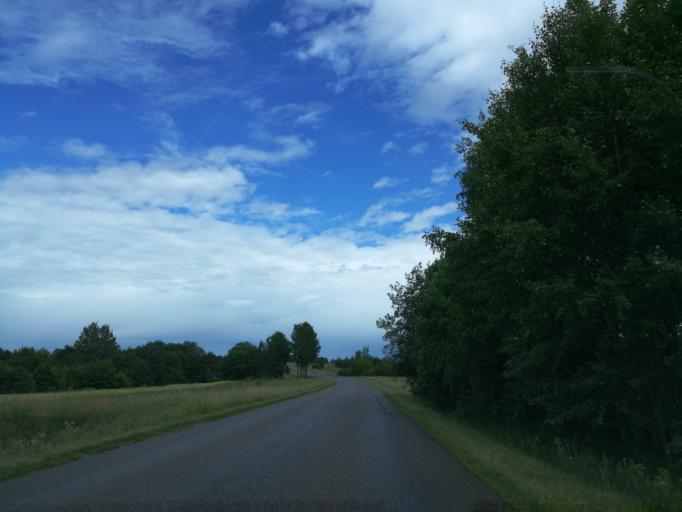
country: LT
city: Trakai
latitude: 54.6732
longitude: 24.9350
